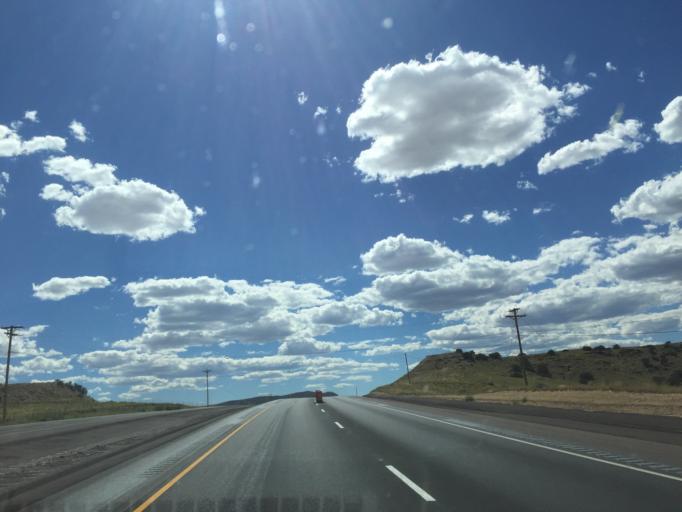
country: US
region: New Mexico
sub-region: McKinley County
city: Twin Lakes
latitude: 35.8643
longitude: -108.7279
